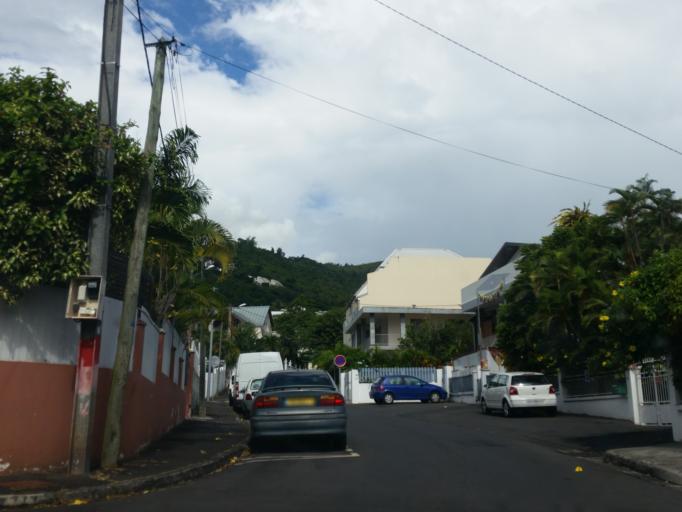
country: RE
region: Reunion
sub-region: Reunion
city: Saint-Denis
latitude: -20.8977
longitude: 55.4561
